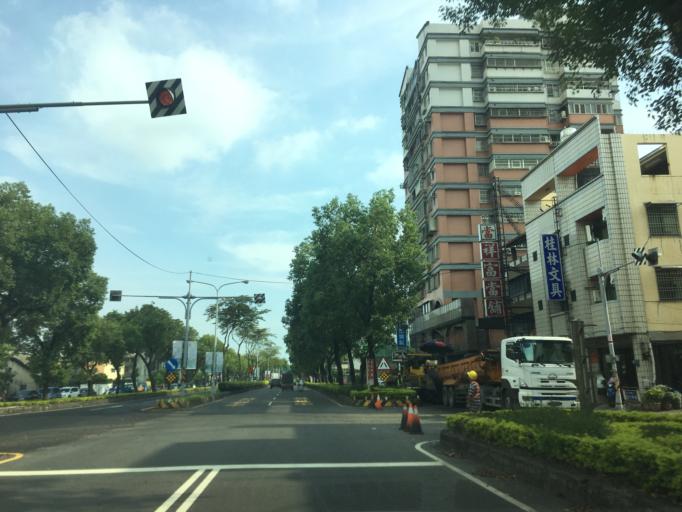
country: TW
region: Taiwan
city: Zhongxing New Village
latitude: 23.9832
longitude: 120.6816
